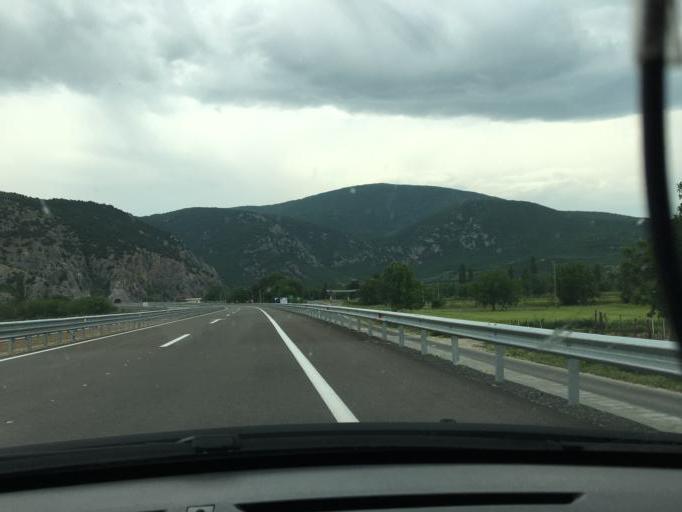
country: MK
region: Demir Kapija
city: Demir Kapija
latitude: 41.4130
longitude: 22.2446
